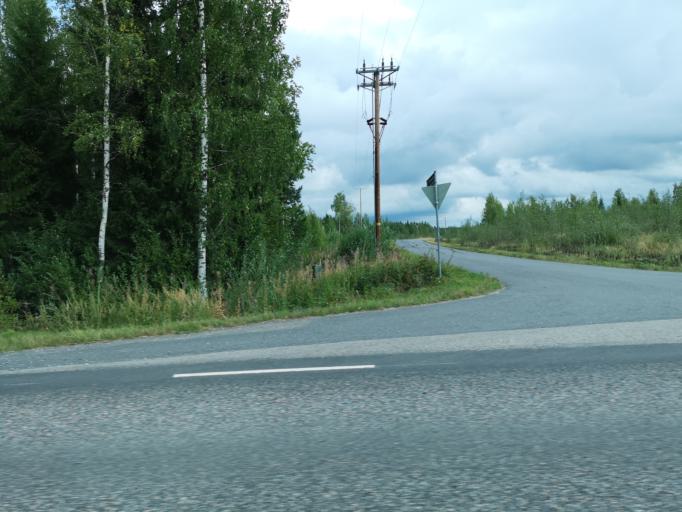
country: FI
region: Central Finland
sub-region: Jyvaeskylae
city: Hankasalmi
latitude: 62.3666
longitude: 26.4477
